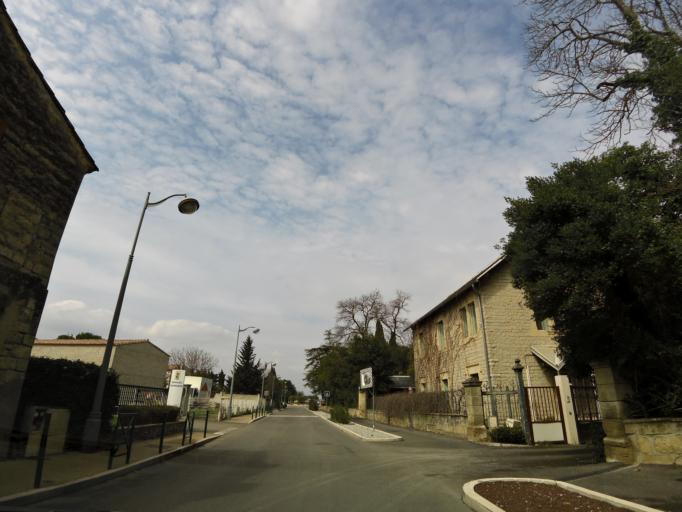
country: FR
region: Languedoc-Roussillon
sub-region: Departement du Gard
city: Aimargues
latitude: 43.6898
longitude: 4.2069
